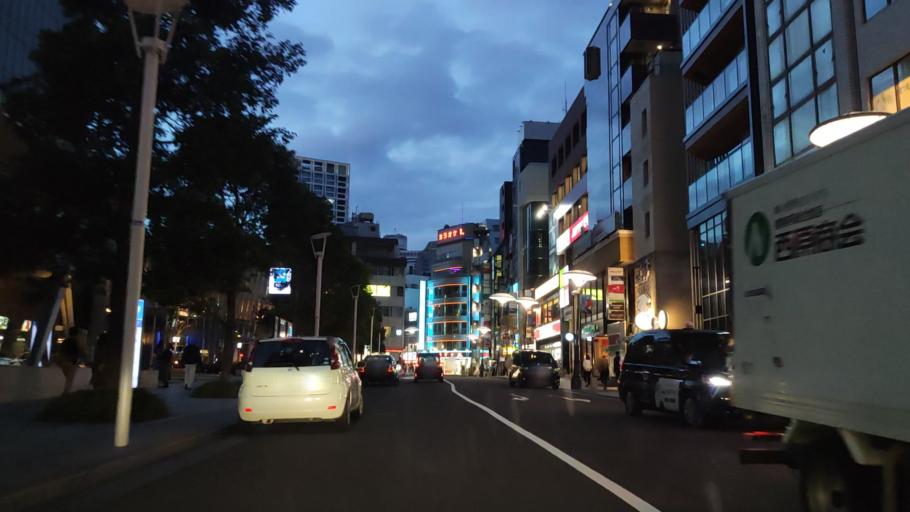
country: JP
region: Tokyo
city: Tokyo
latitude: 35.6729
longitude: 139.7371
